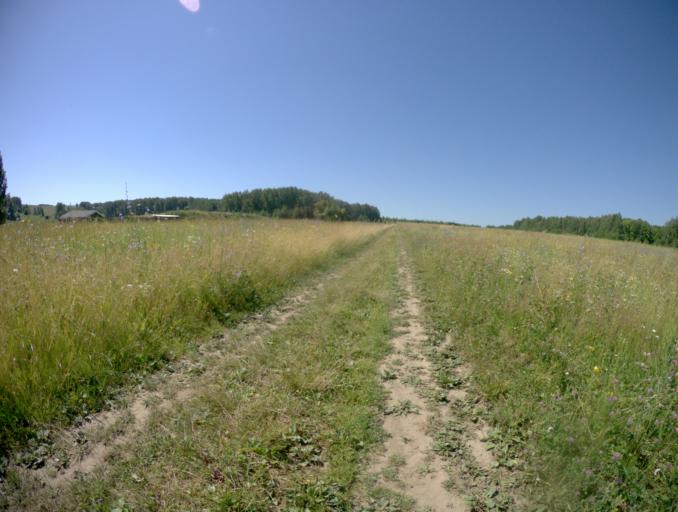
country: RU
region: Nizjnij Novgorod
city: Reshetikha
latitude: 56.1279
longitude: 43.2689
